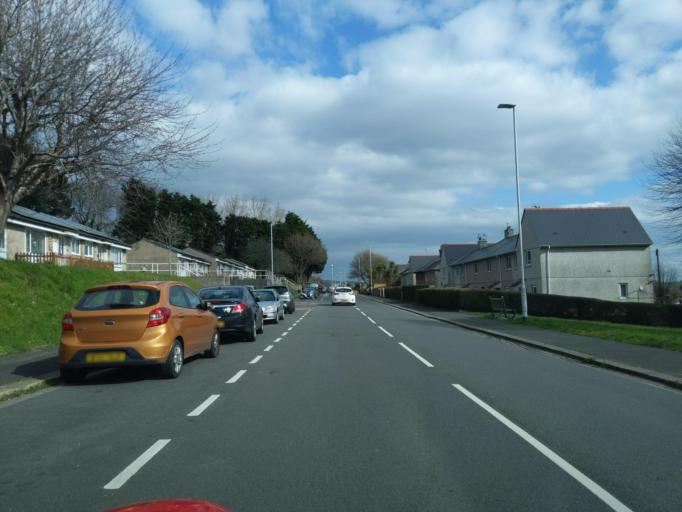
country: GB
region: England
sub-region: Plymouth
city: Plymouth
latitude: 50.3769
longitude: -4.1144
